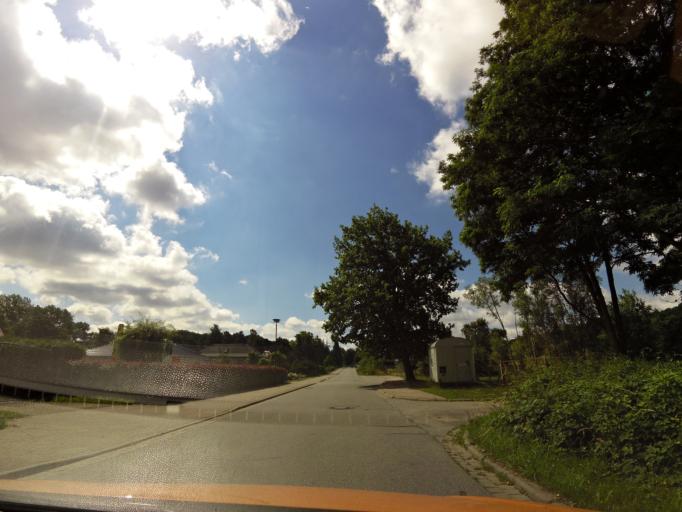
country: DE
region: Mecklenburg-Vorpommern
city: Plau am See
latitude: 53.4441
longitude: 12.2833
